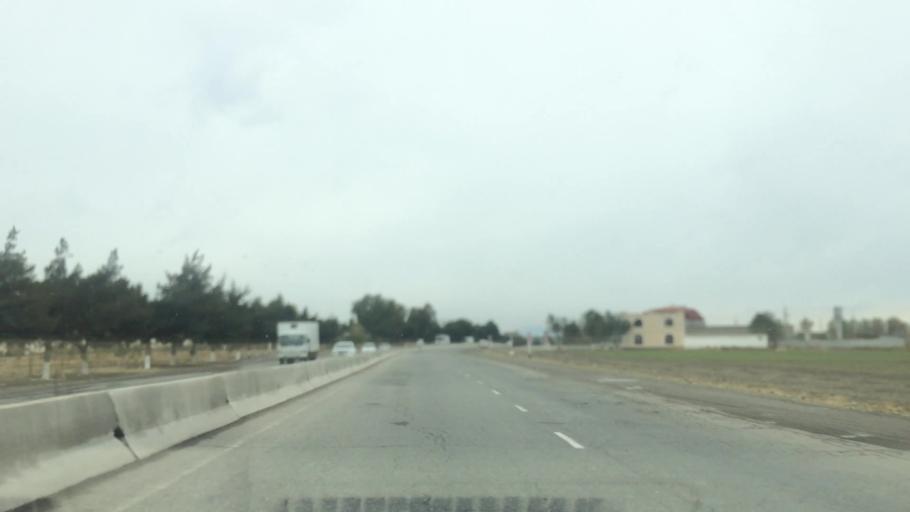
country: UZ
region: Samarqand
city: Bulung'ur
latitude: 39.7592
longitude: 67.2499
